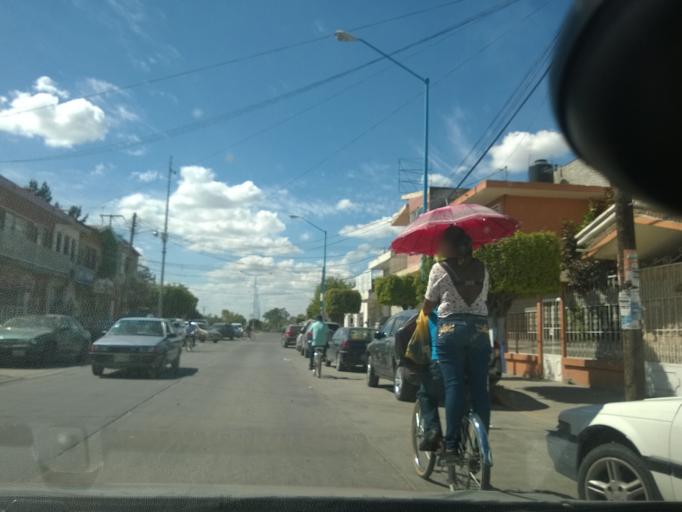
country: MX
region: Guanajuato
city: Romita
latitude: 20.8723
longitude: -101.5207
